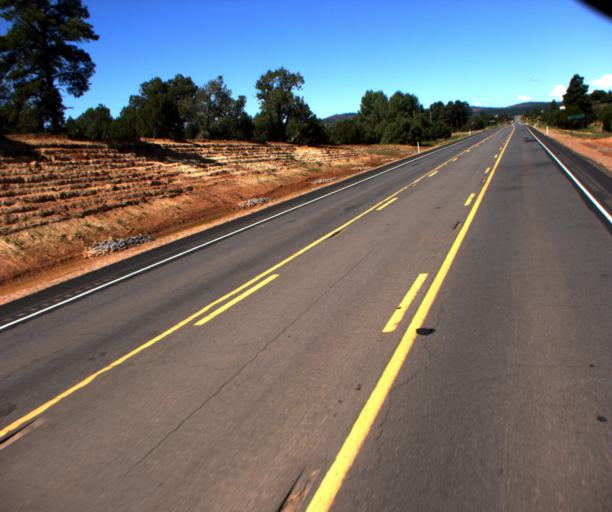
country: US
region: Arizona
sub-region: Navajo County
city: Linden
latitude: 34.2854
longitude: -110.1261
